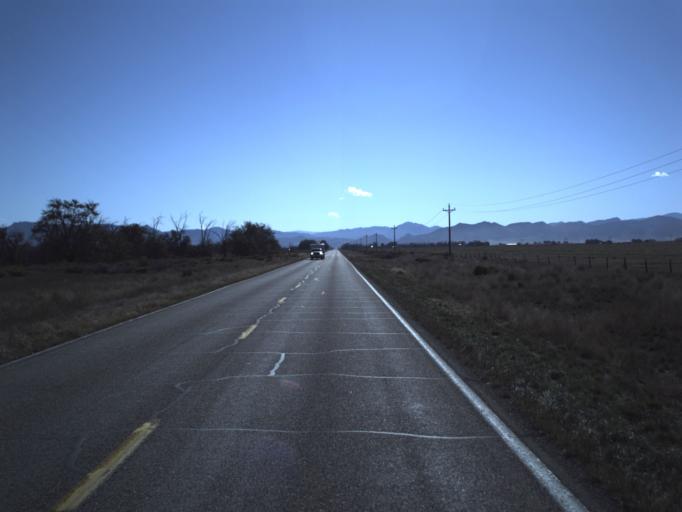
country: US
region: Utah
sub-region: Washington County
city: Enterprise
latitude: 37.7202
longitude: -113.6861
